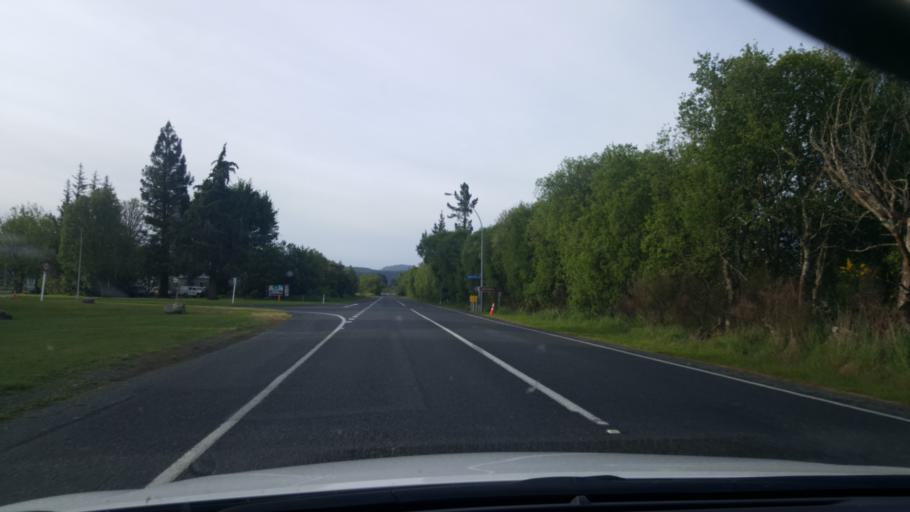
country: NZ
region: Waikato
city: Turangi
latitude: -38.9696
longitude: 175.7691
